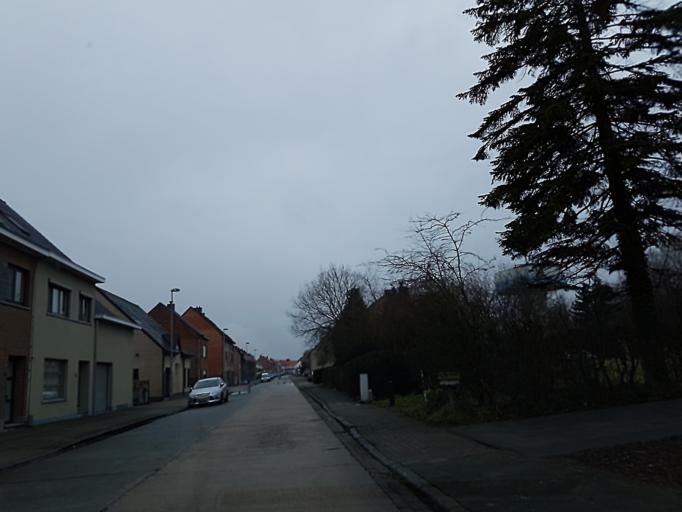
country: BE
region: Flanders
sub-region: Provincie Antwerpen
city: Sint-Amands
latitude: 51.0585
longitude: 4.2148
